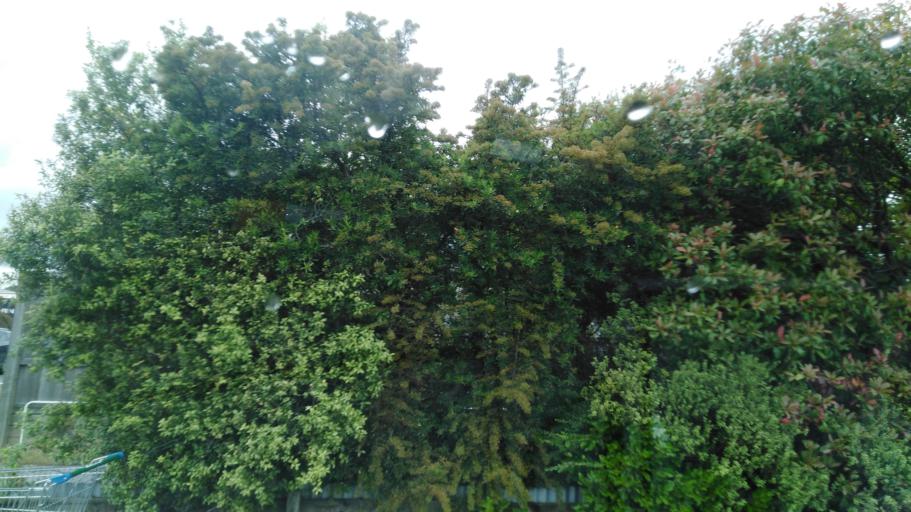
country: NZ
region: Marlborough
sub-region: Marlborough District
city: Blenheim
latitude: -41.5093
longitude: 173.9362
